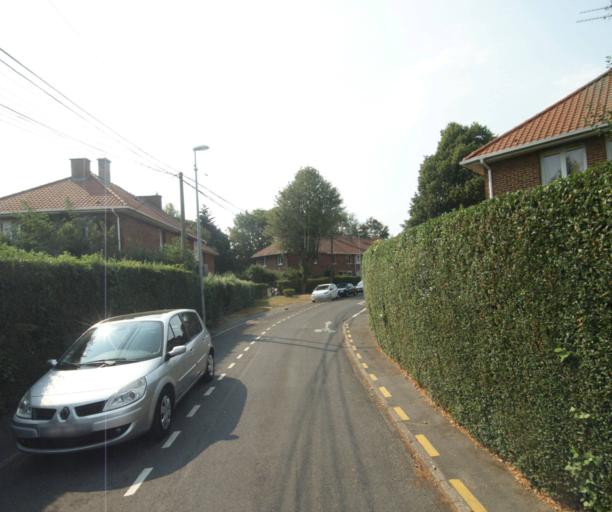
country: FR
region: Nord-Pas-de-Calais
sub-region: Departement du Nord
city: Roncq
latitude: 50.7278
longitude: 3.1319
